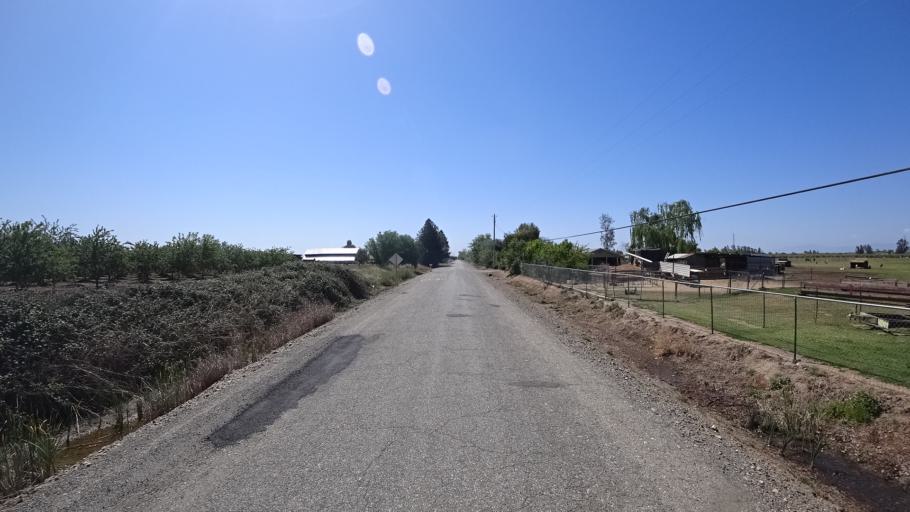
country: US
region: California
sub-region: Glenn County
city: Orland
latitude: 39.7960
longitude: -122.1504
